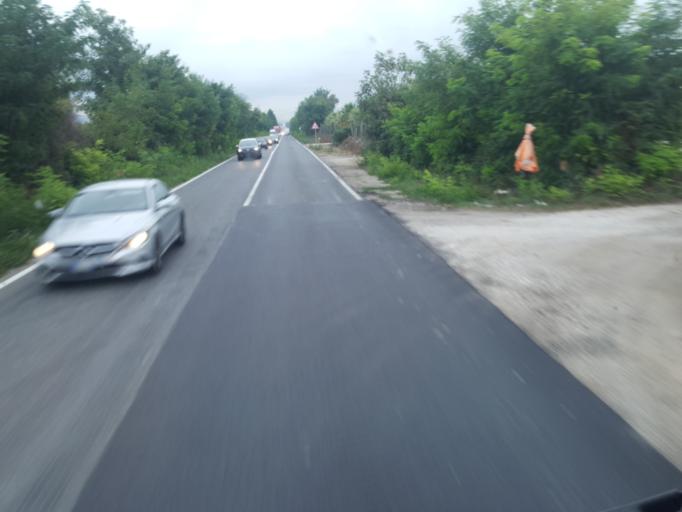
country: IT
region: Campania
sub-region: Provincia di Caserta
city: Pignataro Maggiore
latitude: 41.1696
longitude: 14.1460
